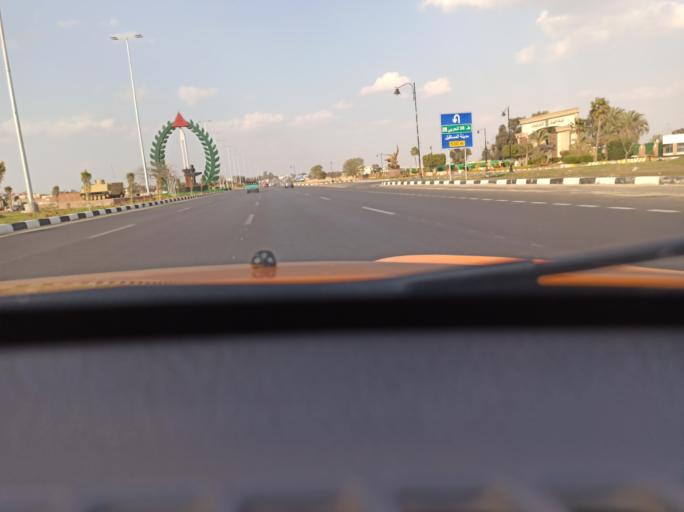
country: EG
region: Al Isma'iliyah
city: Ismailia
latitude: 30.6066
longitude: 32.2139
